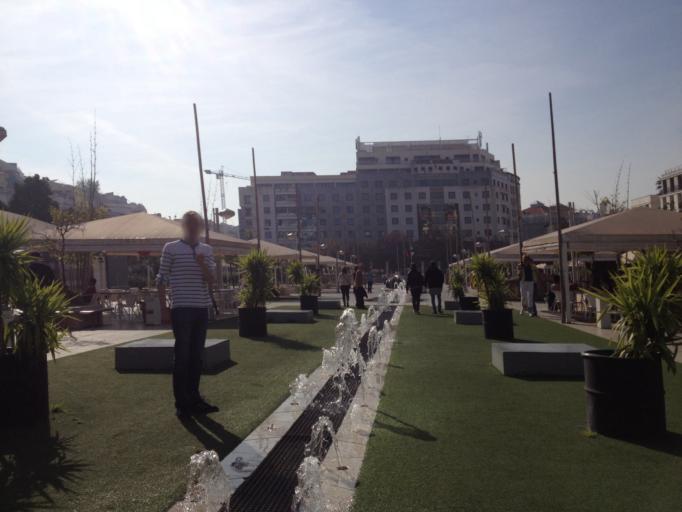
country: PT
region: Lisbon
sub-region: Lisbon
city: Lisbon
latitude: 38.7164
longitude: -9.1363
